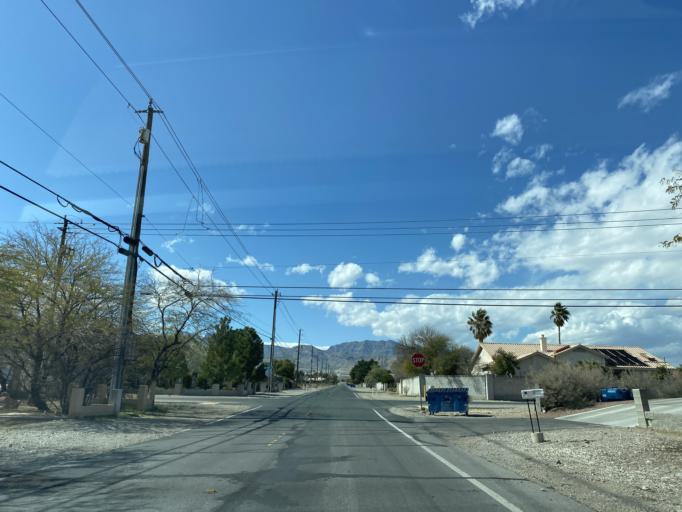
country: US
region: Nevada
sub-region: Clark County
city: Summerlin South
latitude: 36.2556
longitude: -115.2878
